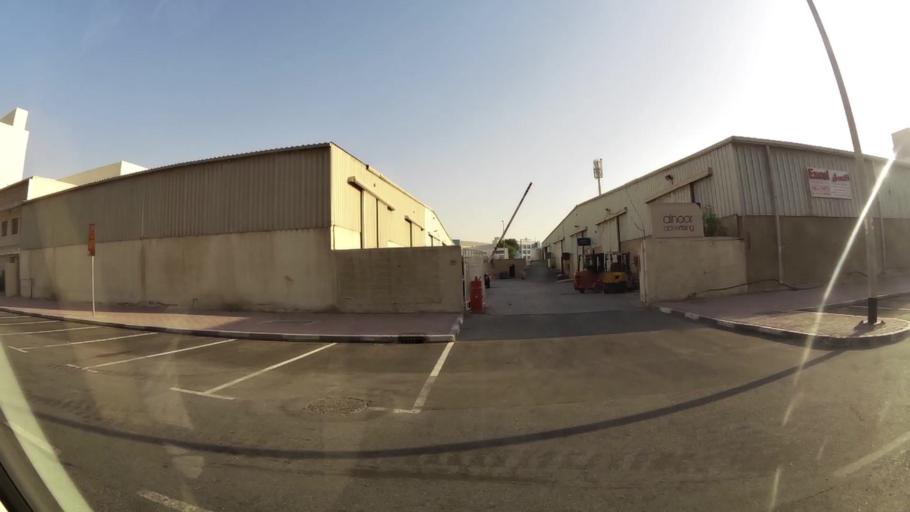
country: AE
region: Ash Shariqah
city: Sharjah
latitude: 25.2524
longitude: 55.3415
